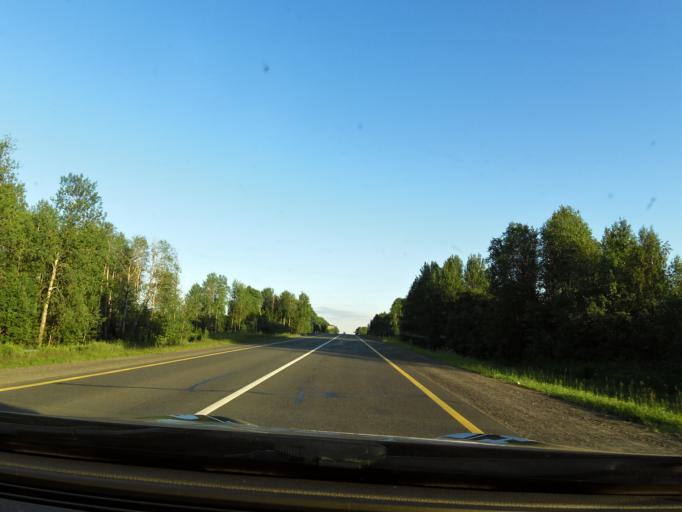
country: RU
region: Vologda
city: Gryazovets
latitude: 58.7826
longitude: 40.2716
